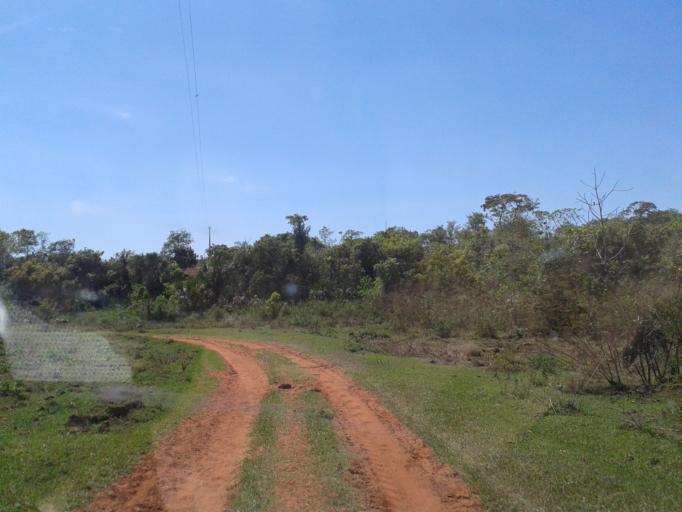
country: BR
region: Minas Gerais
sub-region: Monte Alegre De Minas
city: Monte Alegre de Minas
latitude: -18.7980
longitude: -49.0739
